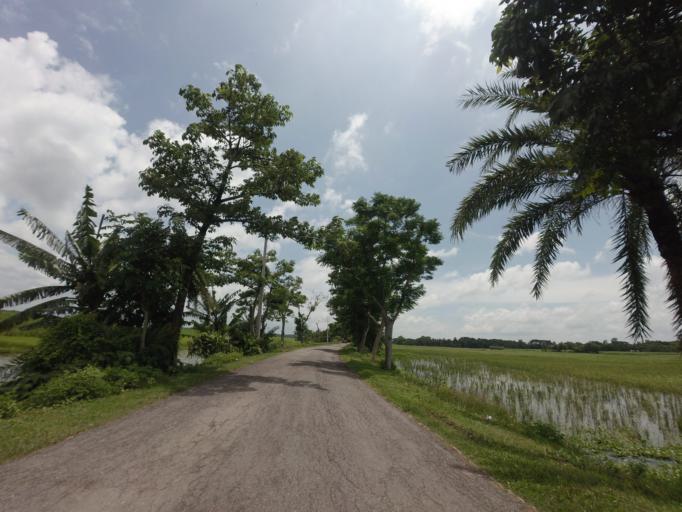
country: BD
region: Khulna
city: Kalia
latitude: 23.0421
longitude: 89.6497
